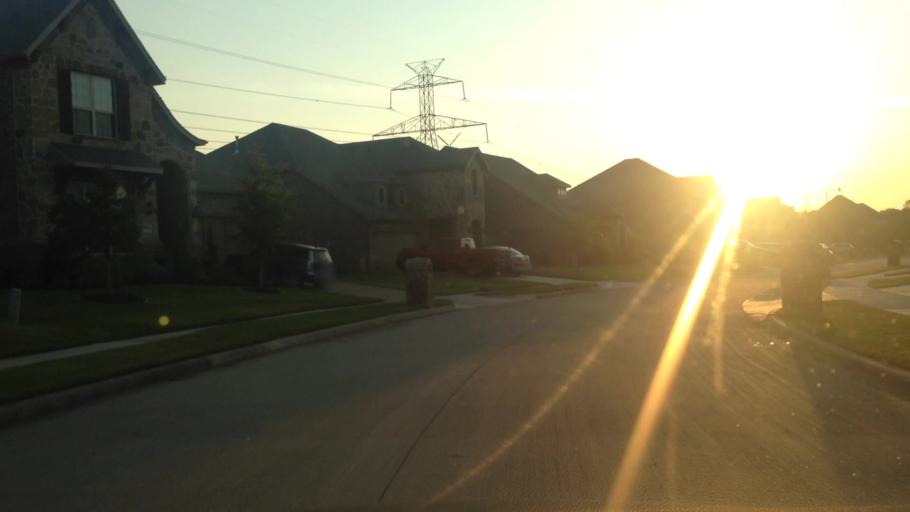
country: US
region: Texas
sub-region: Tarrant County
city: Kennedale
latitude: 32.6314
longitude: -97.1904
